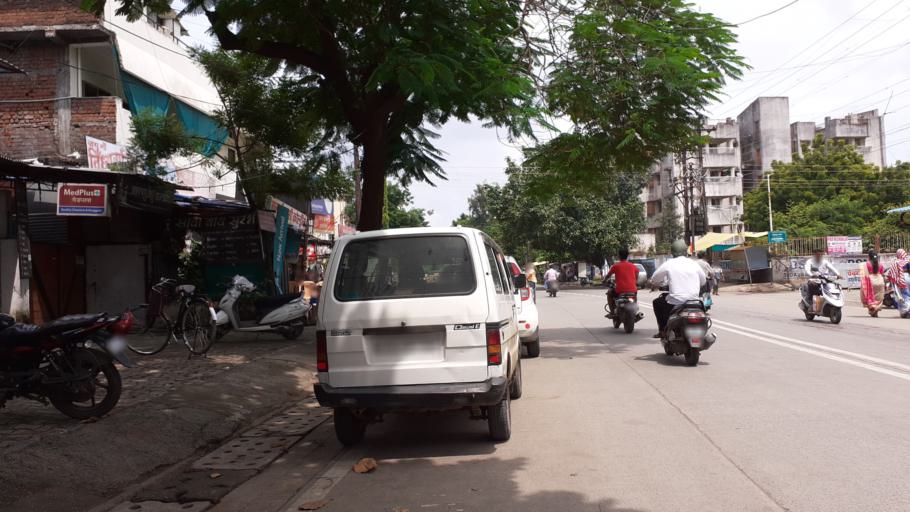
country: IN
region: Maharashtra
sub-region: Nagpur Division
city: Nagpur
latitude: 21.1174
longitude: 79.1111
